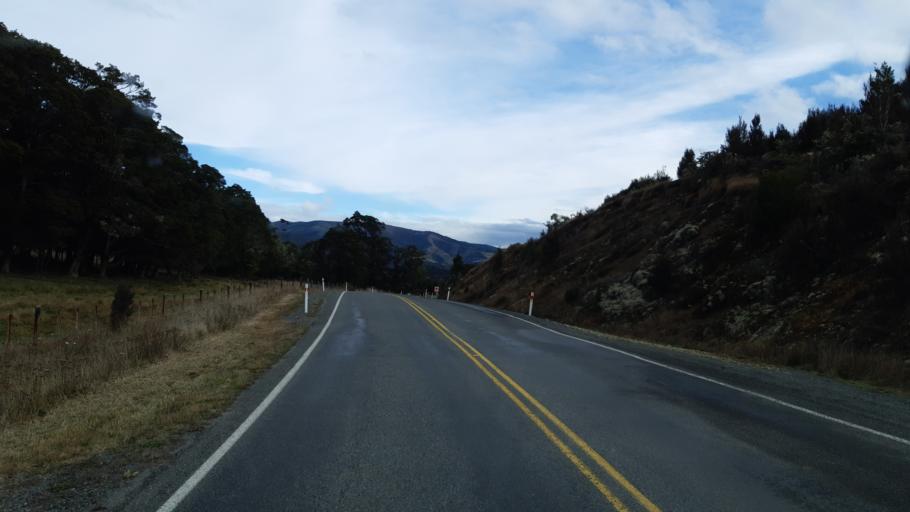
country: NZ
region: Tasman
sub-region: Tasman District
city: Wakefield
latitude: -41.7997
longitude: 172.8651
